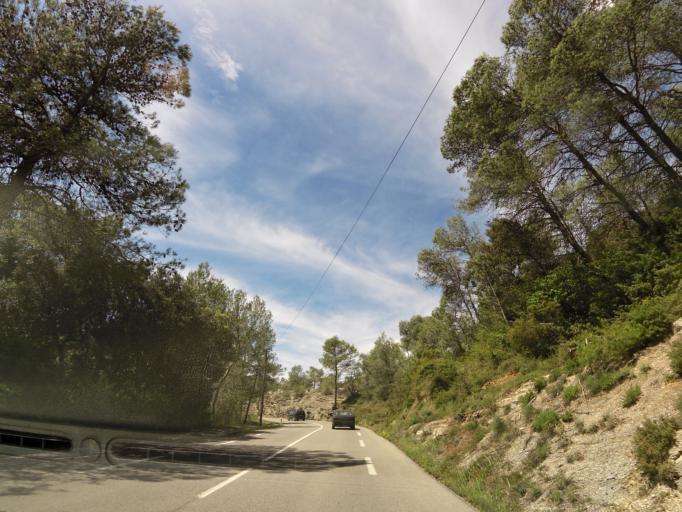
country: FR
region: Languedoc-Roussillon
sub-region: Departement du Gard
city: Quissac
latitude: 43.8422
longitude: 4.0246
